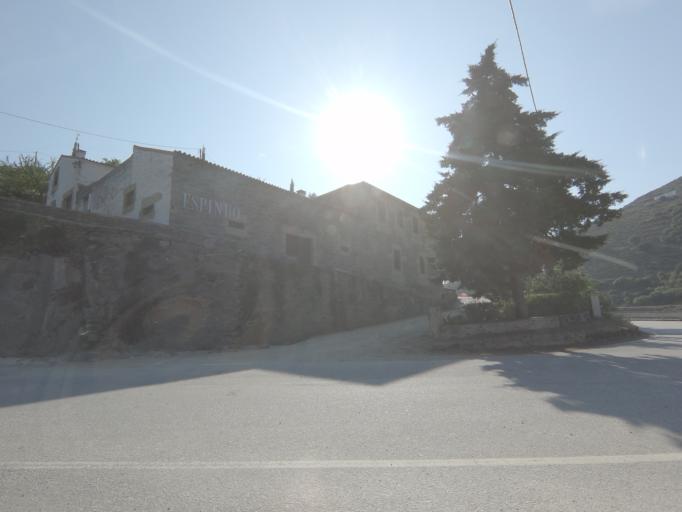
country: PT
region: Viseu
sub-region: Tabuaco
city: Tabuaco
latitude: 41.1571
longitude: -7.5828
